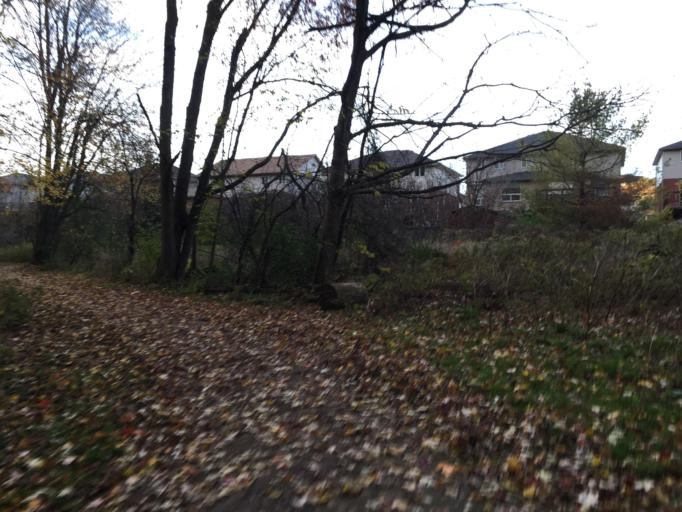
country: CA
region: Ontario
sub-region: Wellington County
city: Guelph
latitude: 43.5277
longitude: -80.3035
